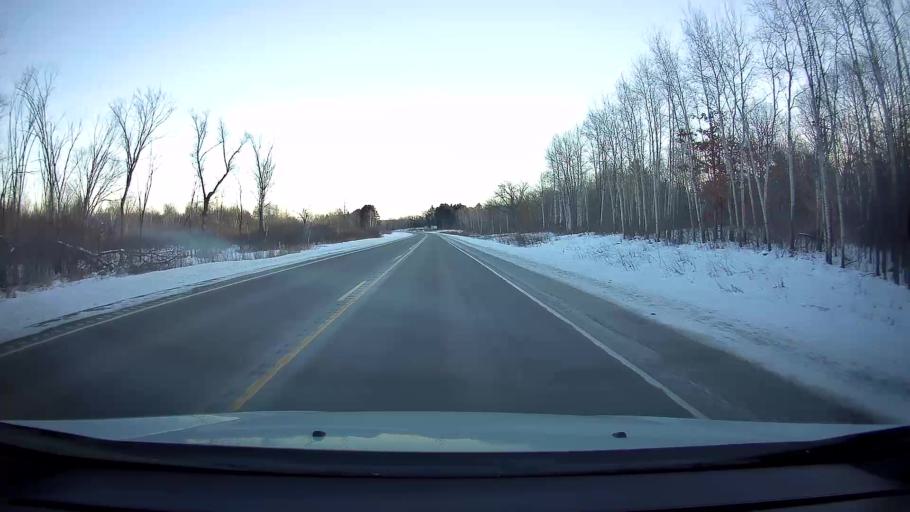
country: US
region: Wisconsin
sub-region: Washburn County
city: Shell Lake
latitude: 45.7056
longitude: -91.9495
